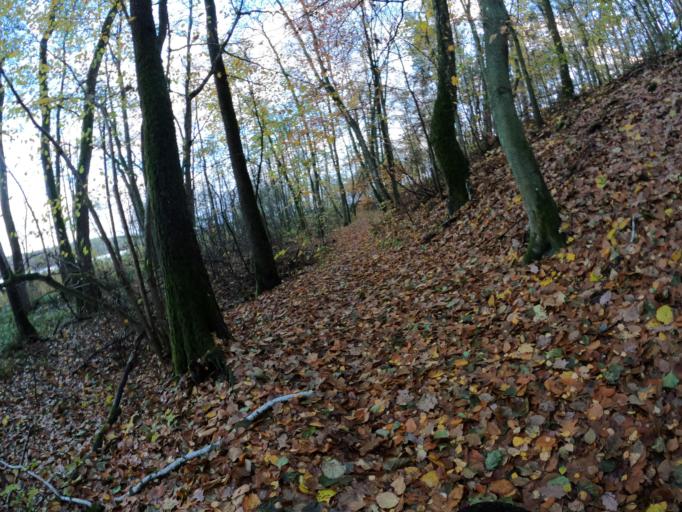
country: PL
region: West Pomeranian Voivodeship
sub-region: Powiat walecki
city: Tuczno
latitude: 53.1882
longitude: 16.1702
